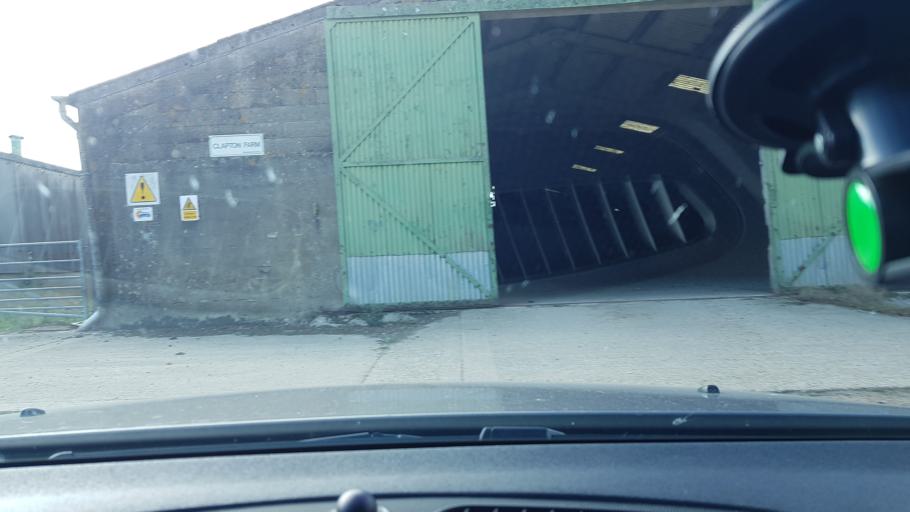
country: GB
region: England
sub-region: West Berkshire
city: Wickham
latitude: 51.4276
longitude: -1.4504
